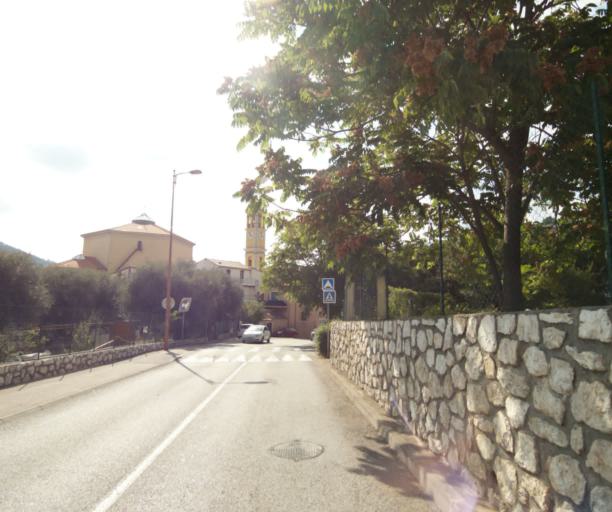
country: FR
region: Provence-Alpes-Cote d'Azur
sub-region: Departement des Alpes-Maritimes
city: La Trinite
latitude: 43.7439
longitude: 7.3153
